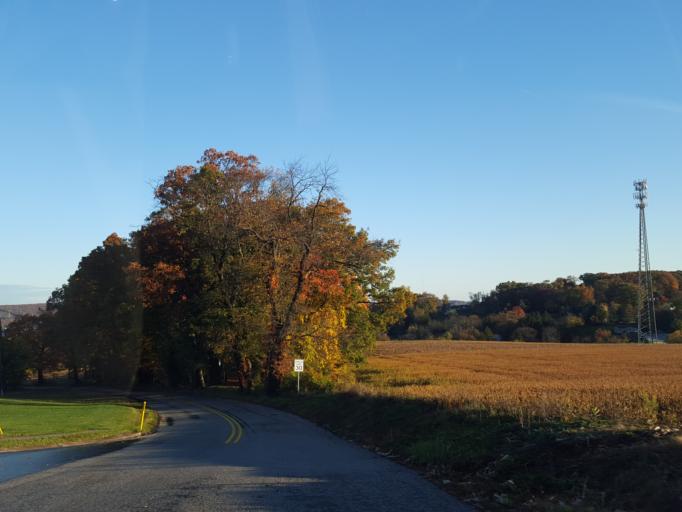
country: US
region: Pennsylvania
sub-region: York County
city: Stonybrook
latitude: 39.9661
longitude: -76.6270
